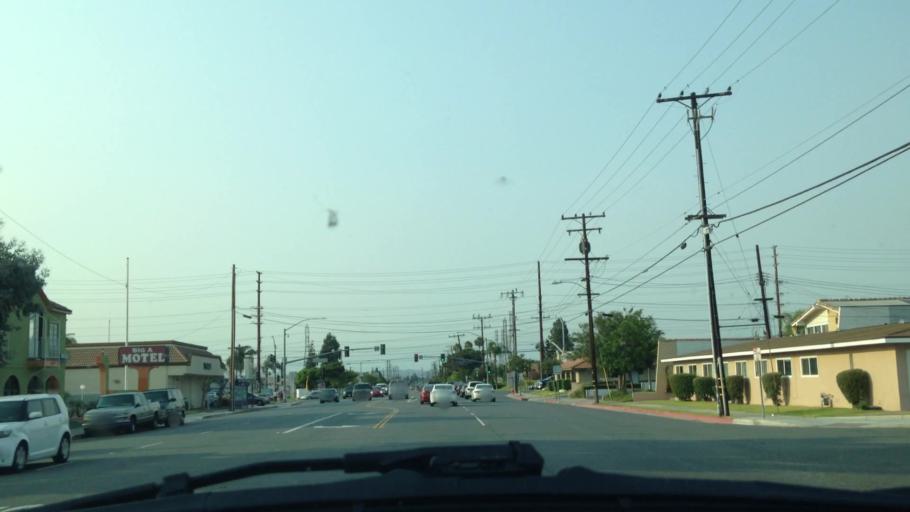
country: US
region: California
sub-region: Orange County
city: Orange
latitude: 33.8077
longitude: -117.8530
